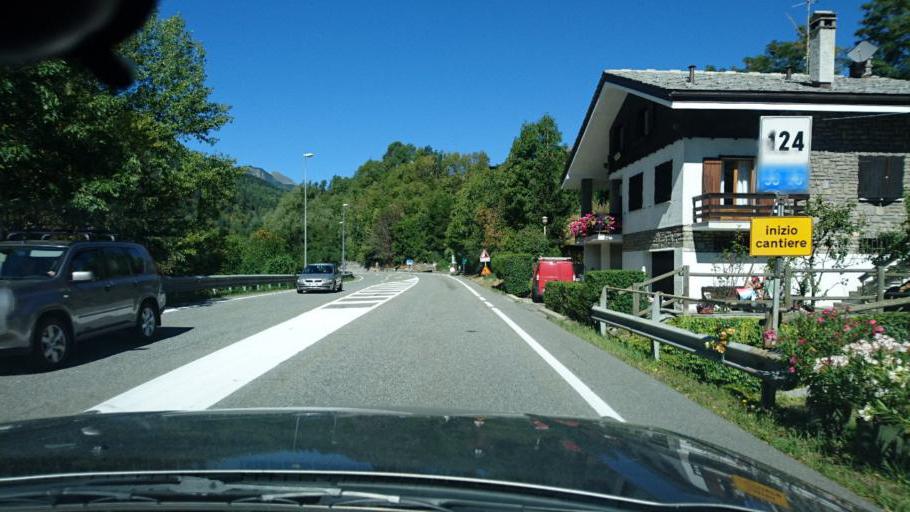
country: IT
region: Aosta Valley
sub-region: Valle d'Aosta
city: La Salle
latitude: 45.7299
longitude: 7.0859
